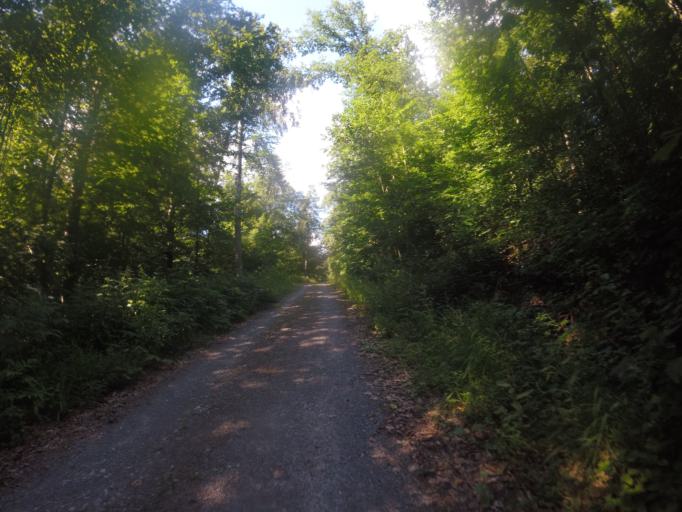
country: DE
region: Baden-Wuerttemberg
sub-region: Regierungsbezirk Stuttgart
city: Oberstenfeld
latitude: 49.0154
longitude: 9.3553
